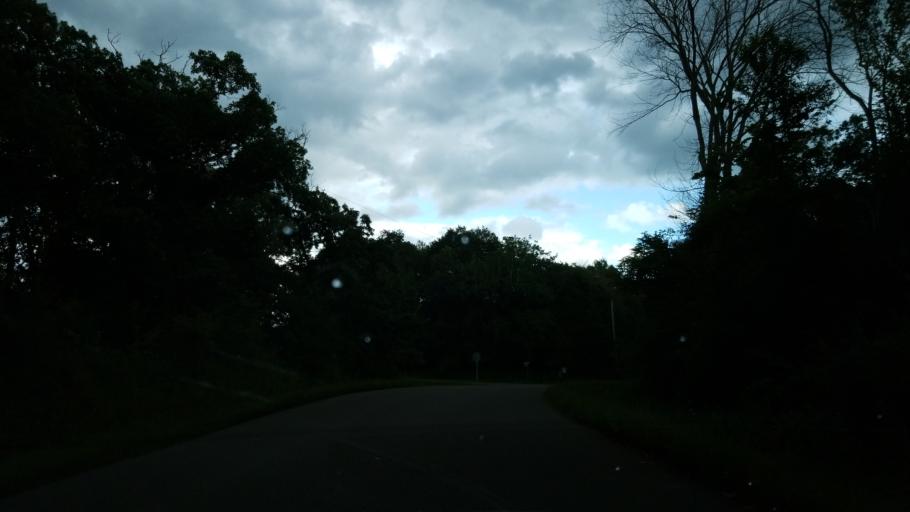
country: US
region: Minnesota
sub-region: Washington County
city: Afton
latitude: 44.8824
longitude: -92.7564
